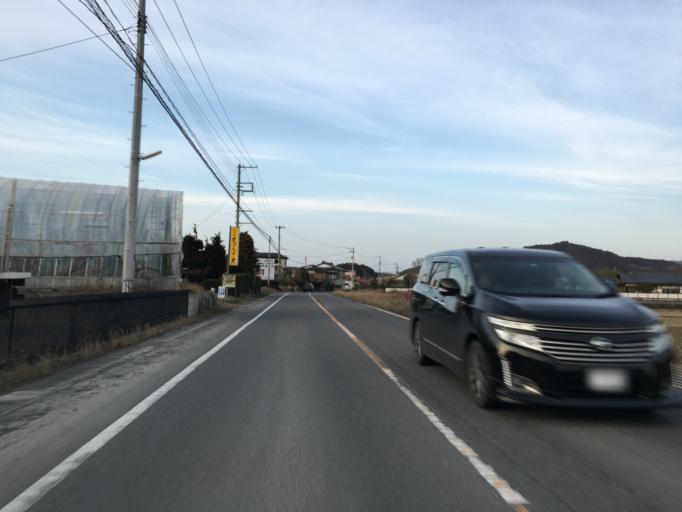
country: JP
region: Ibaraki
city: Daigo
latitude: 36.9392
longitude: 140.4053
